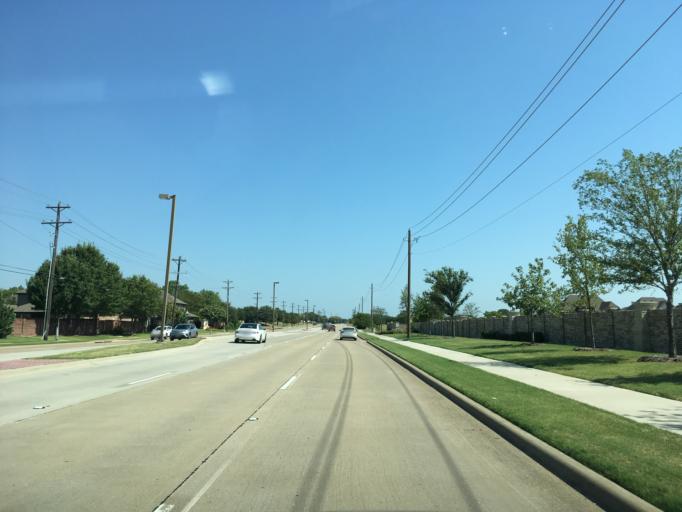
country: US
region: Texas
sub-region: Collin County
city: Fairview
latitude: 33.1528
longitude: -96.6806
